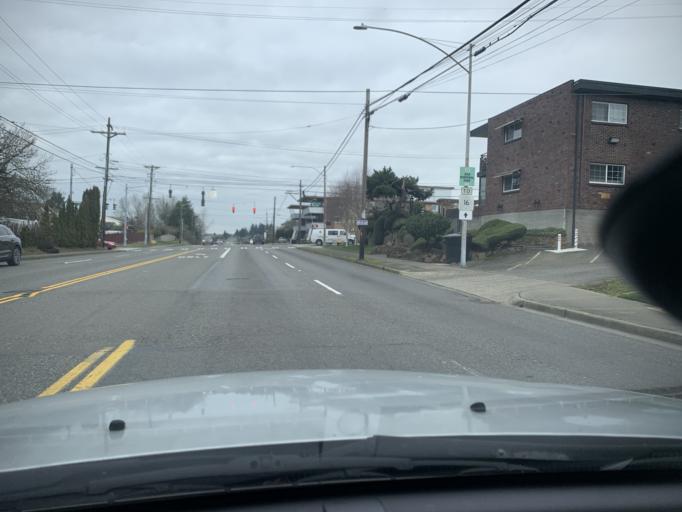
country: US
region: Washington
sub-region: Pierce County
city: University Place
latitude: 47.2549
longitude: -122.5369
